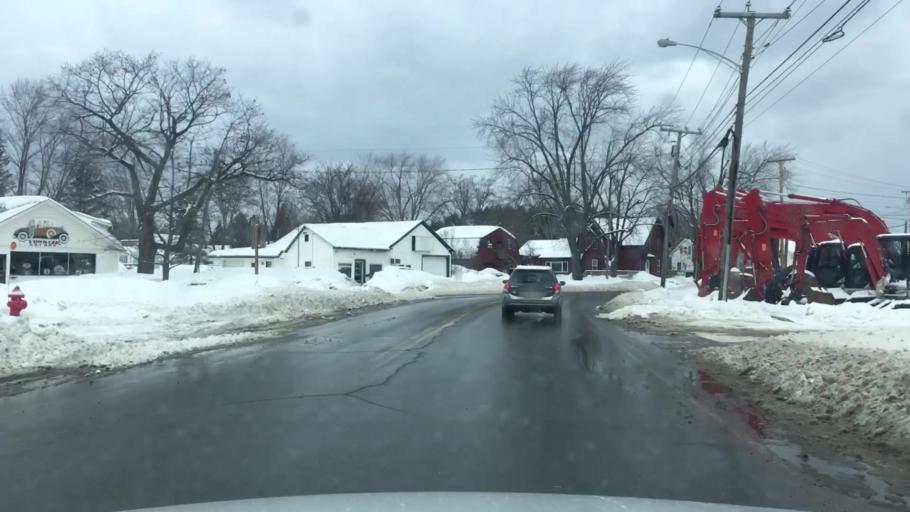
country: US
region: Maine
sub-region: Somerset County
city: Skowhegan
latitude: 44.7773
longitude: -69.7200
